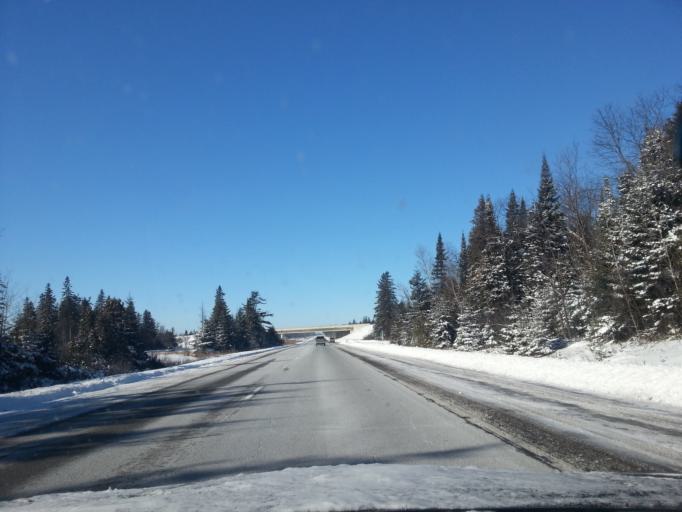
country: CA
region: Ontario
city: Carleton Place
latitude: 45.3321
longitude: -76.1571
